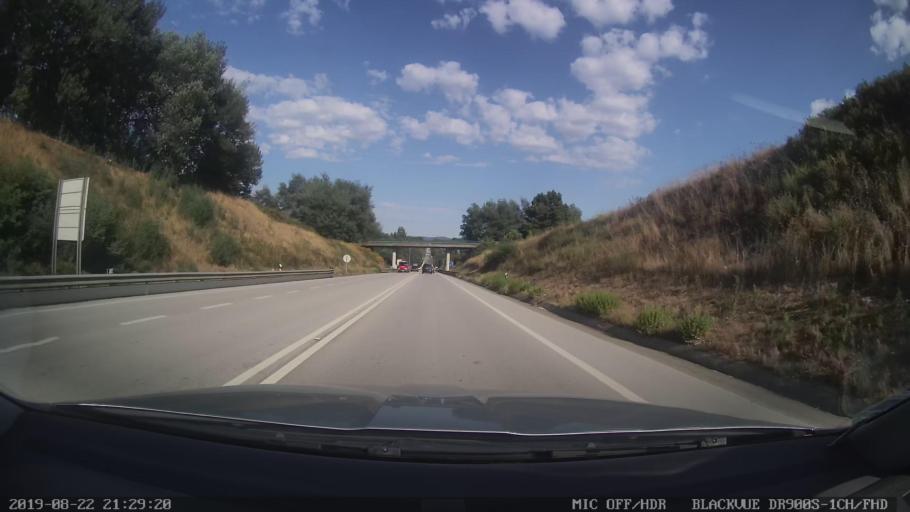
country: PT
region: Leiria
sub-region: Pedrogao Grande
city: Pedrogao Grande
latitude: 39.9014
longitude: -8.1334
